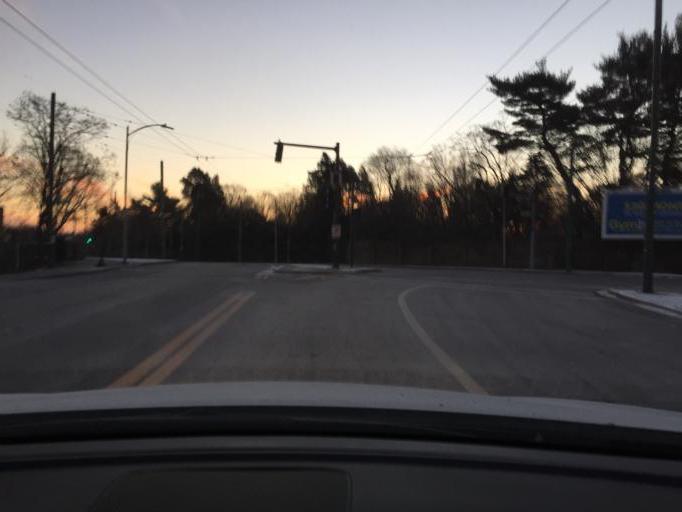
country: US
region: Massachusetts
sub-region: Middlesex County
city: Watertown
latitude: 42.3747
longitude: -71.1505
